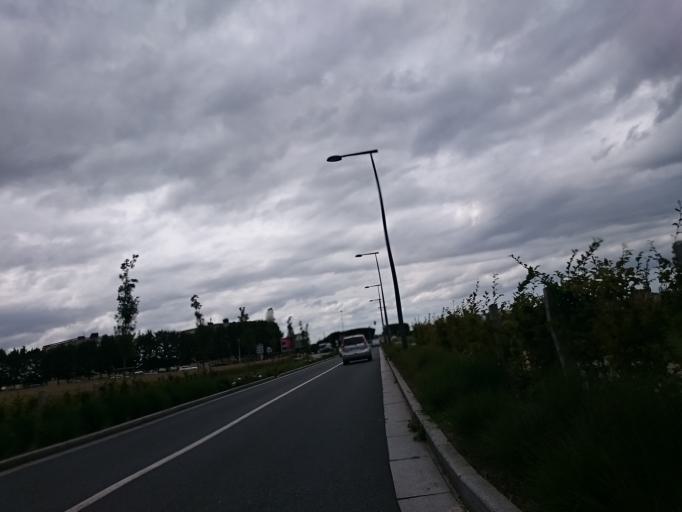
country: FR
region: Lower Normandy
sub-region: Departement du Calvados
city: Fleury-sur-Orne
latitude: 49.1442
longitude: -0.3722
